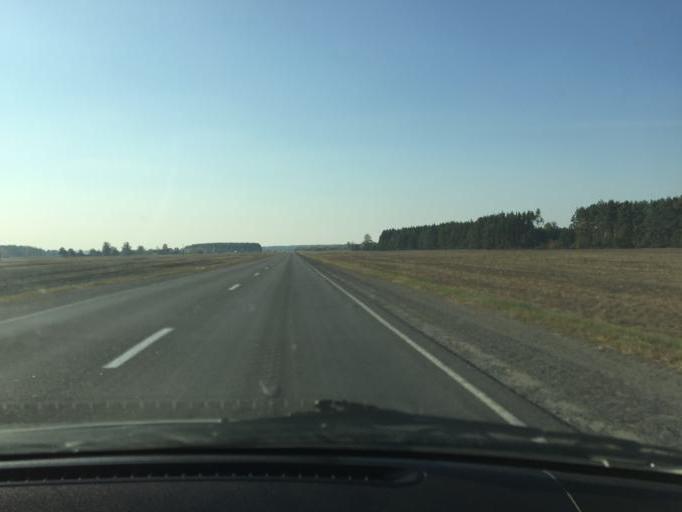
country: BY
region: Brest
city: Davyd-Haradok
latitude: 52.2400
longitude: 27.2067
